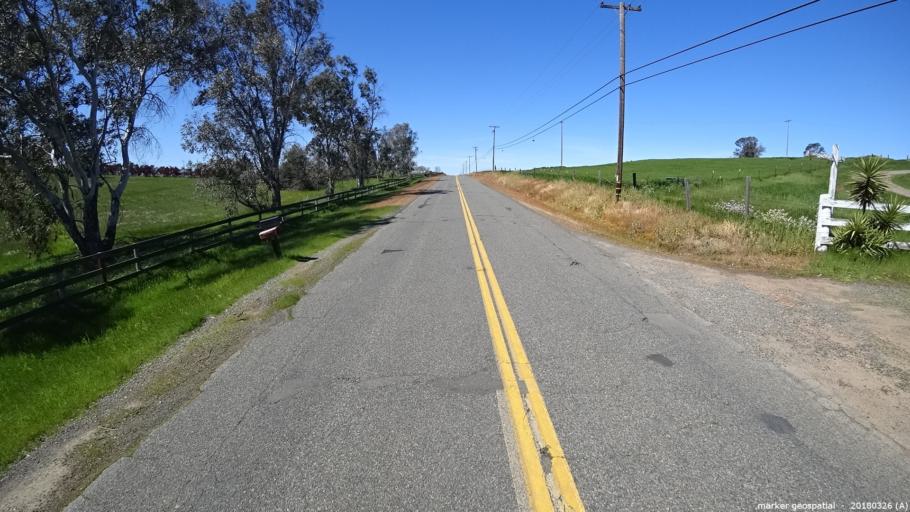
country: US
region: California
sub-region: Sacramento County
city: Wilton
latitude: 38.4644
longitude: -121.2419
